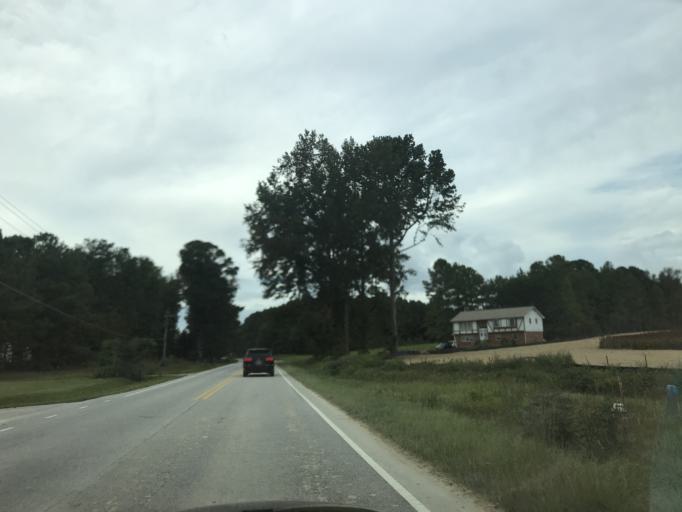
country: US
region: North Carolina
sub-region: Franklin County
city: Youngsville
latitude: 35.9999
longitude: -78.4264
